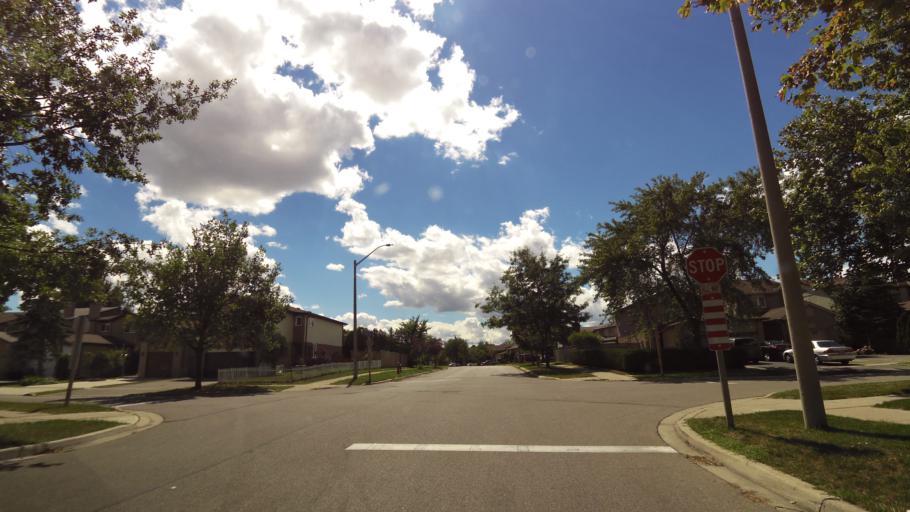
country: CA
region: Ontario
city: Mississauga
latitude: 43.6172
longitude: -79.6226
